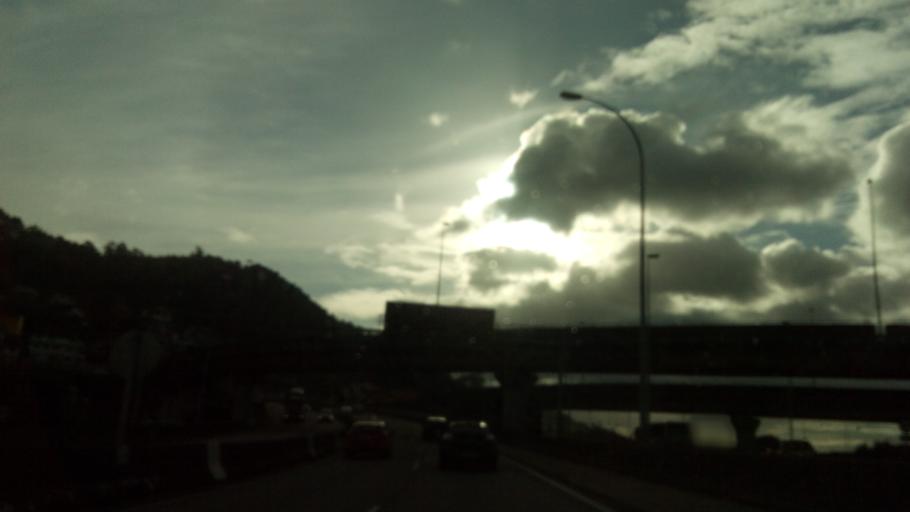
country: ES
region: Galicia
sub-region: Provincia de Pontevedra
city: Vigo
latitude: 42.2598
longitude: -8.6745
